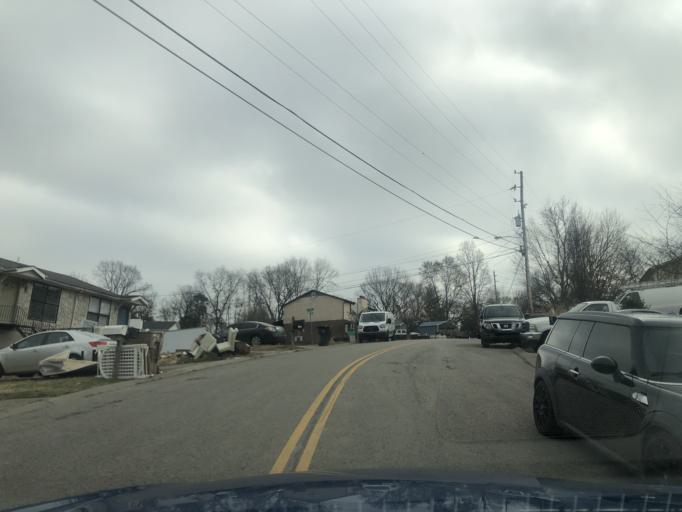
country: US
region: Tennessee
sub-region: Davidson County
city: Oak Hill
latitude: 36.0959
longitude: -86.7107
